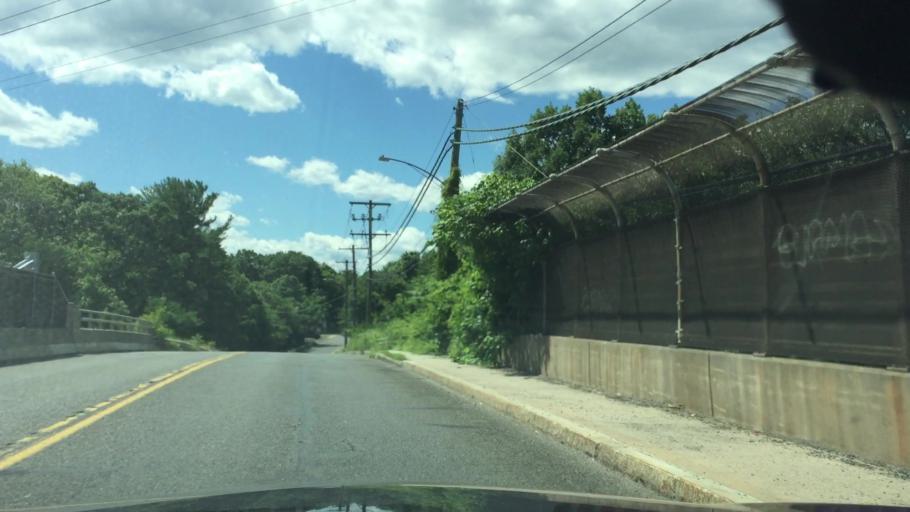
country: US
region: Connecticut
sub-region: New Haven County
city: City of Milford (balance)
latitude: 41.2117
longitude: -73.0853
